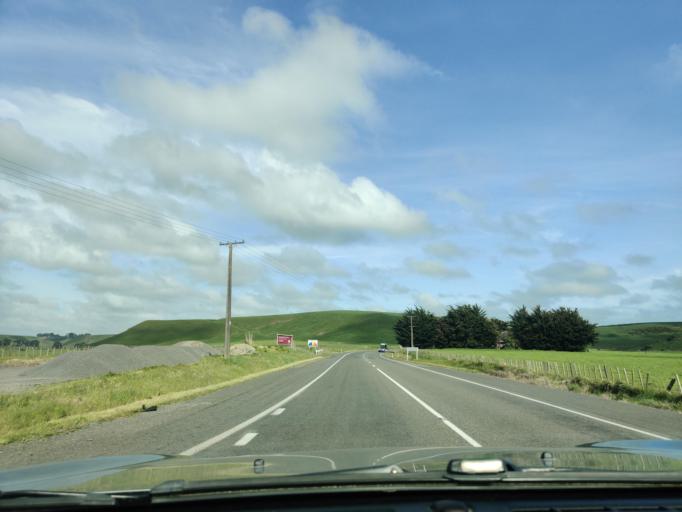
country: NZ
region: Manawatu-Wanganui
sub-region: Wanganui District
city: Wanganui
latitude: -40.0103
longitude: 175.1706
